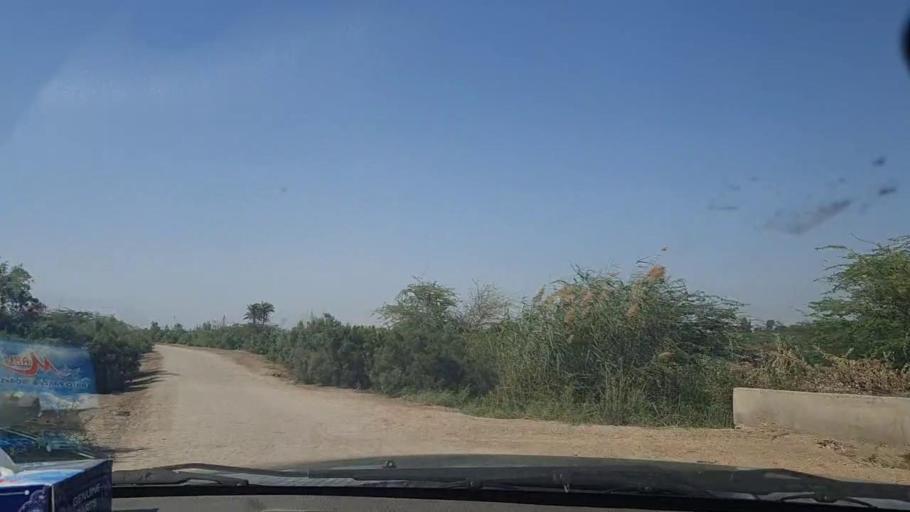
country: PK
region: Sindh
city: Chuhar Jamali
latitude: 24.2858
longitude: 67.7591
